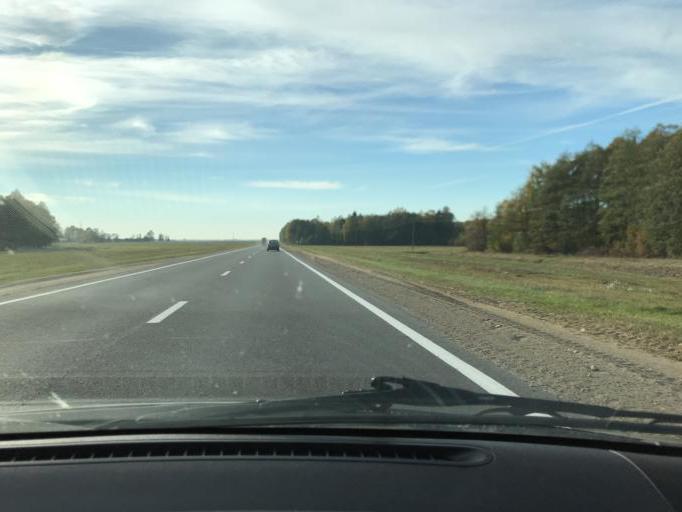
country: BY
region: Brest
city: Ivanava
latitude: 52.1562
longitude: 25.7088
